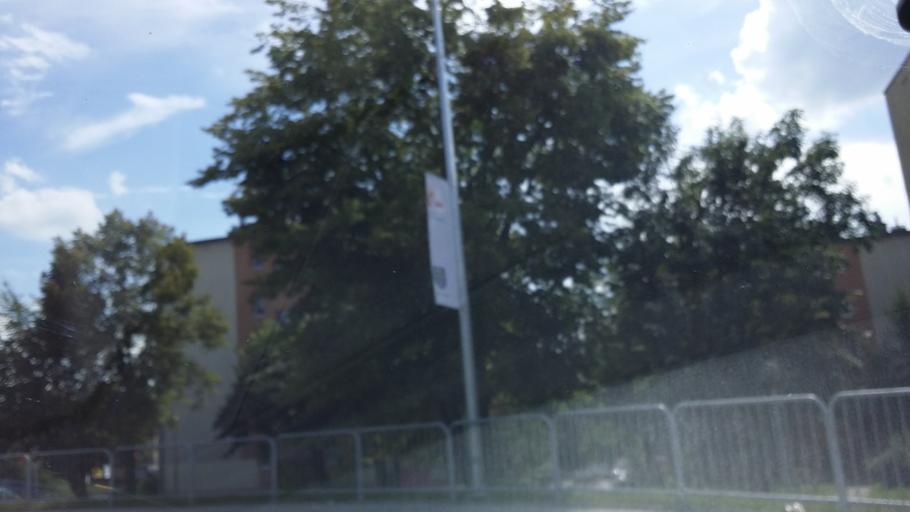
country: PL
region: Lesser Poland Voivodeship
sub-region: Powiat wielicki
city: Wieliczka
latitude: 49.9867
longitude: 20.0709
